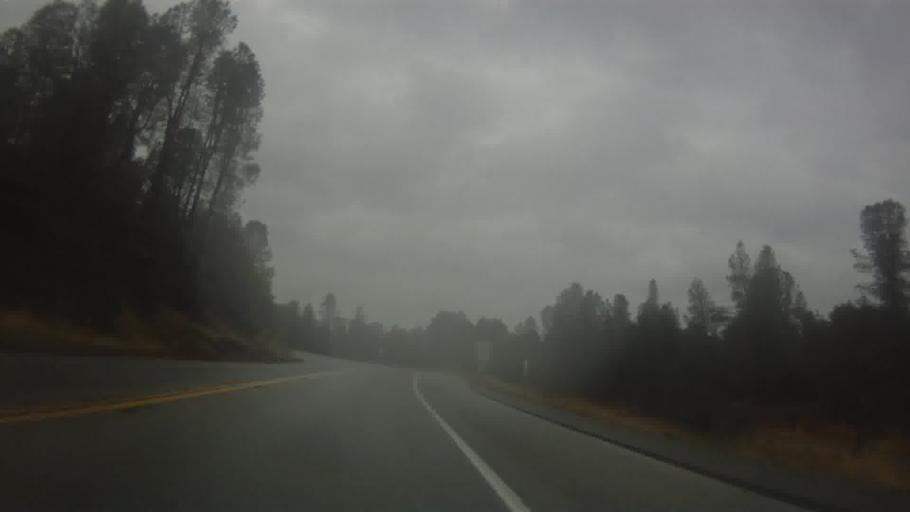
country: US
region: California
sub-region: Shasta County
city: Shasta
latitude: 40.5884
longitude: -122.4575
